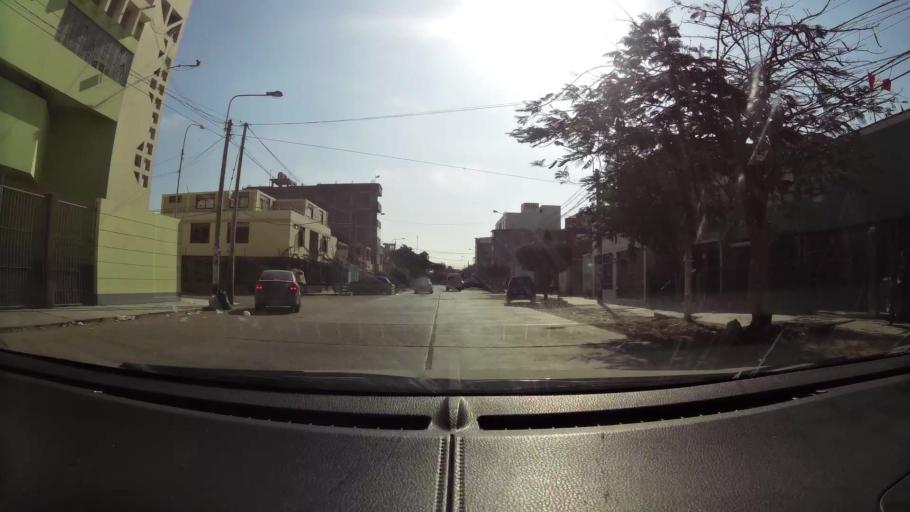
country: PE
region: Lambayeque
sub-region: Provincia de Chiclayo
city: Chiclayo
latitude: -6.7647
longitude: -79.8428
